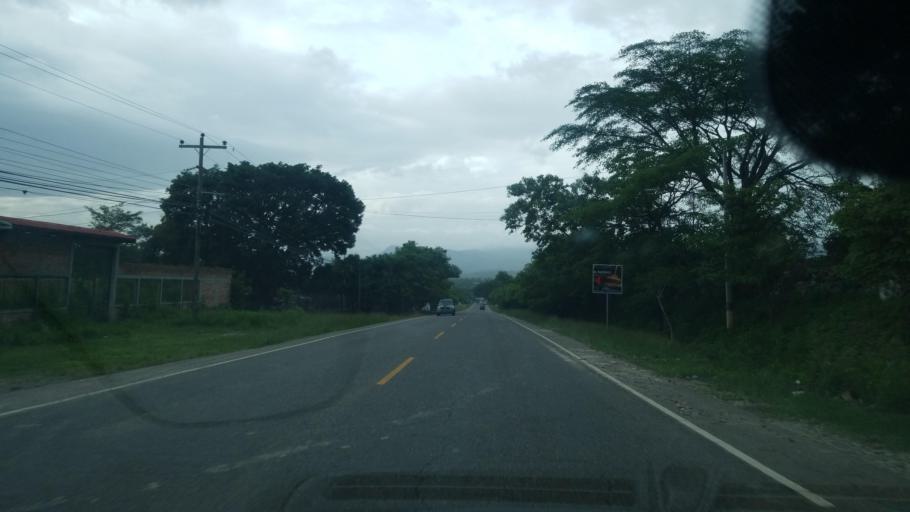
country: HN
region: Ocotepeque
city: Antigua Ocotepeque
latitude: 14.4039
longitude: -89.1958
